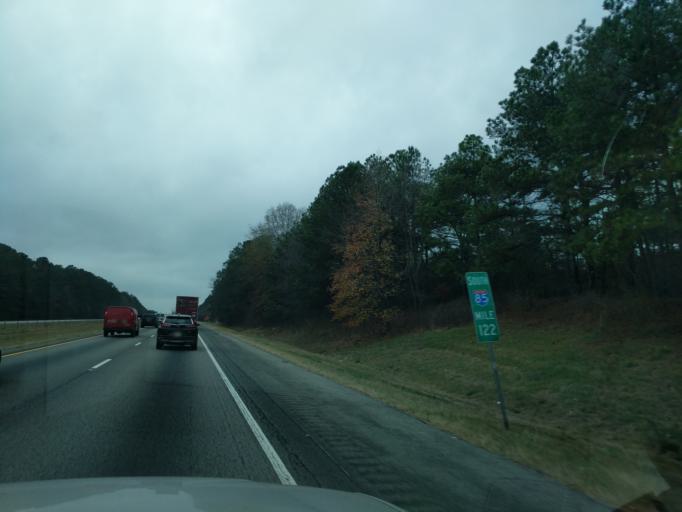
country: US
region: Georgia
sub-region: Barrow County
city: Auburn
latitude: 34.0809
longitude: -83.8787
